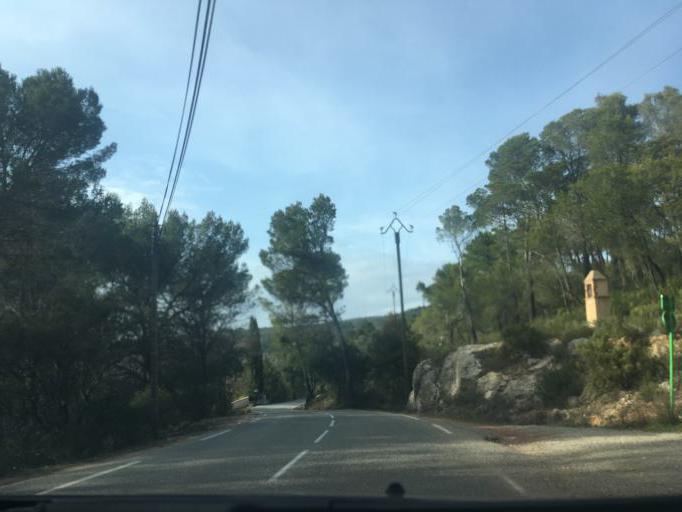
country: FR
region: Provence-Alpes-Cote d'Azur
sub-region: Departement du Var
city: Villecroze
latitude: 43.5749
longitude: 6.2839
